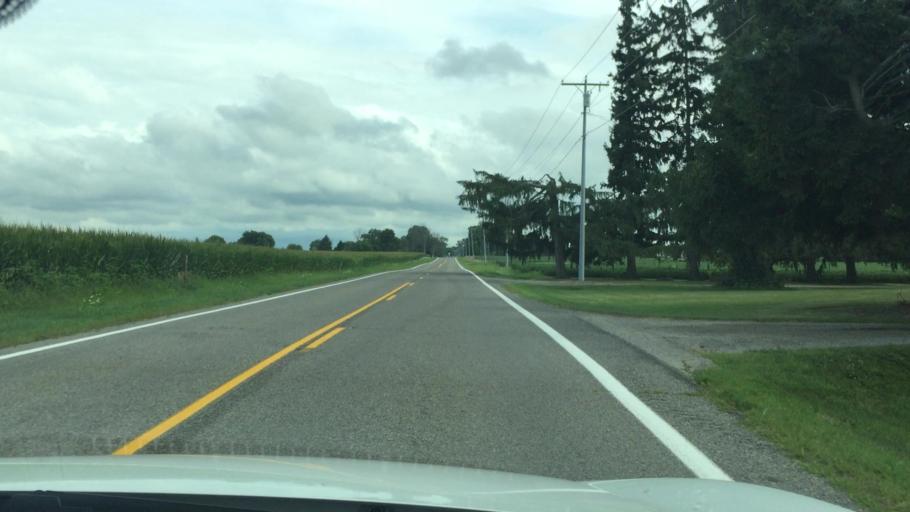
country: US
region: Ohio
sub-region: Champaign County
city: North Lewisburg
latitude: 40.2126
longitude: -83.5435
